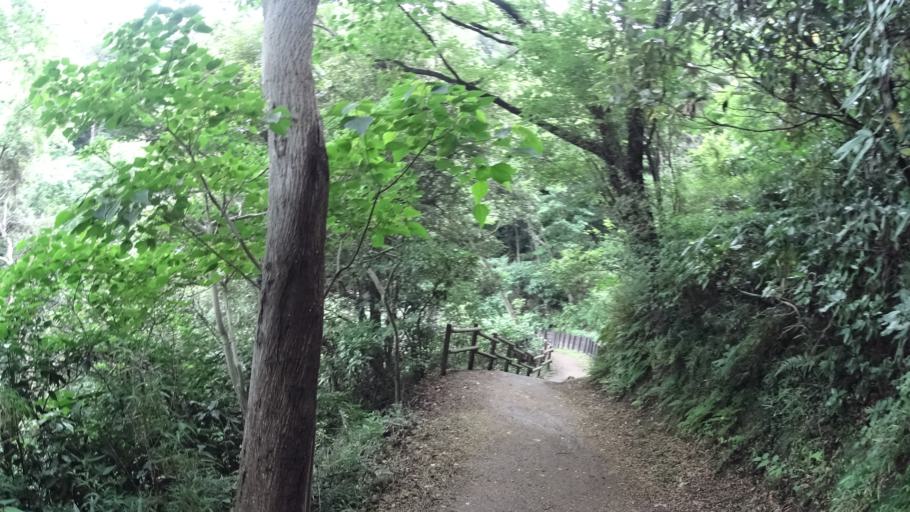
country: JP
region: Kanagawa
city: Zushi
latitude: 35.3543
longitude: 139.6148
